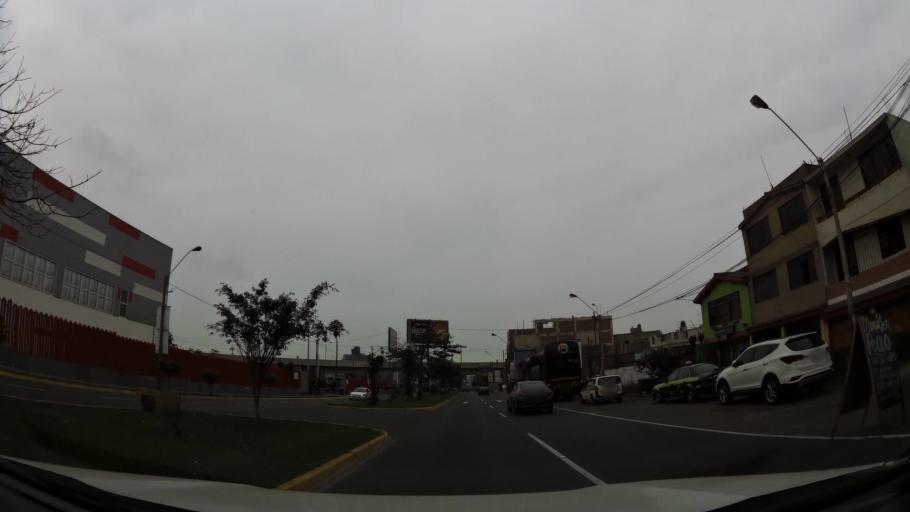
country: PE
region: Lima
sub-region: Lima
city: San Luis
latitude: -12.0807
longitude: -77.0040
